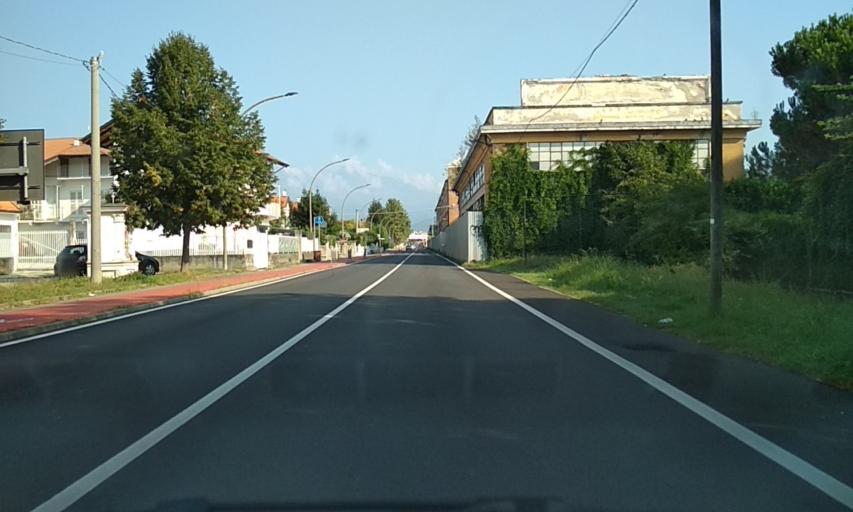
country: IT
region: Piedmont
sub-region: Provincia di Torino
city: Rivarolo Canavese
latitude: 45.3214
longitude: 7.7290
